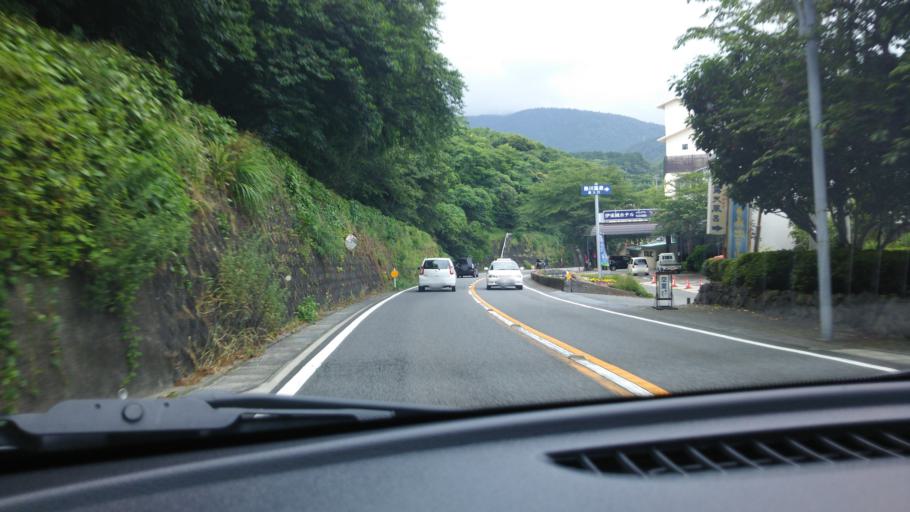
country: JP
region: Shizuoka
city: Ito
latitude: 34.8134
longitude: 139.0687
